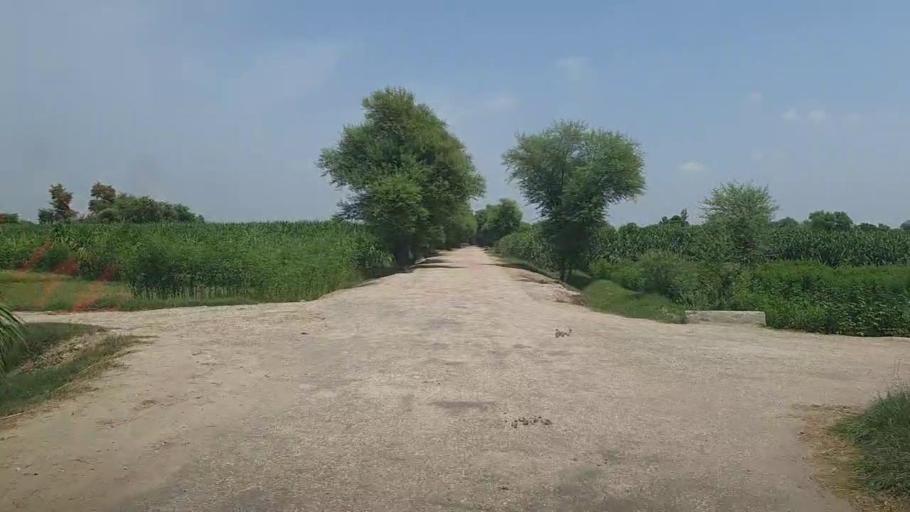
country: PK
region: Sindh
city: Ubauro
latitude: 28.2394
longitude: 69.8210
